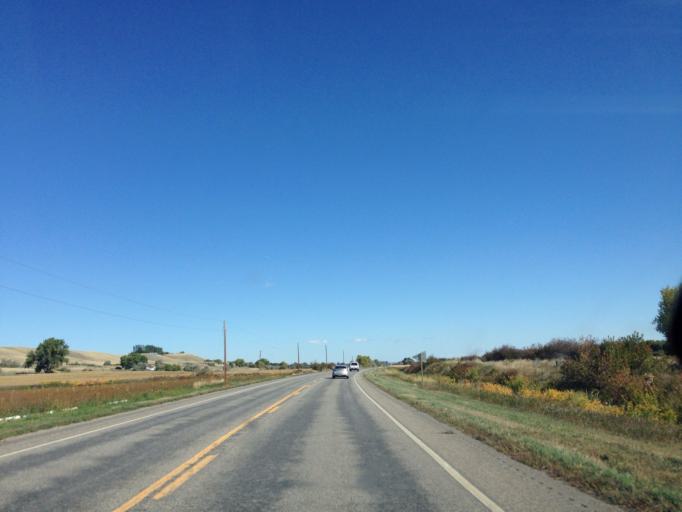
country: US
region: Montana
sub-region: Yellowstone County
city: Laurel
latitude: 45.5759
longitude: -108.8333
